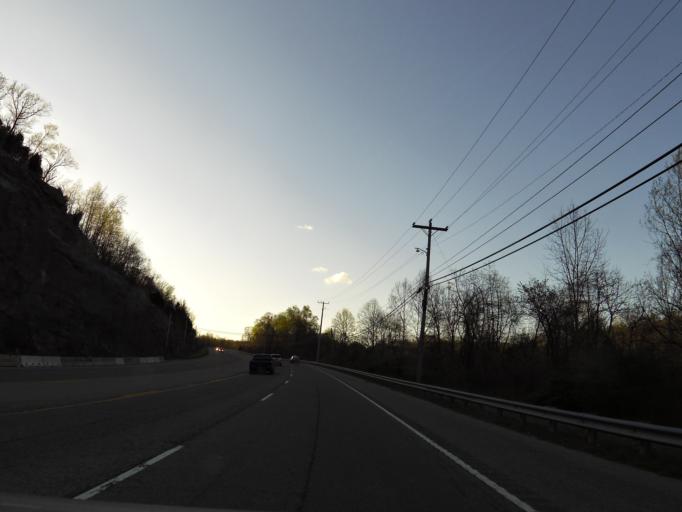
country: US
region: Tennessee
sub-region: Robertson County
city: Ridgetop
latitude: 36.3863
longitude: -86.7557
